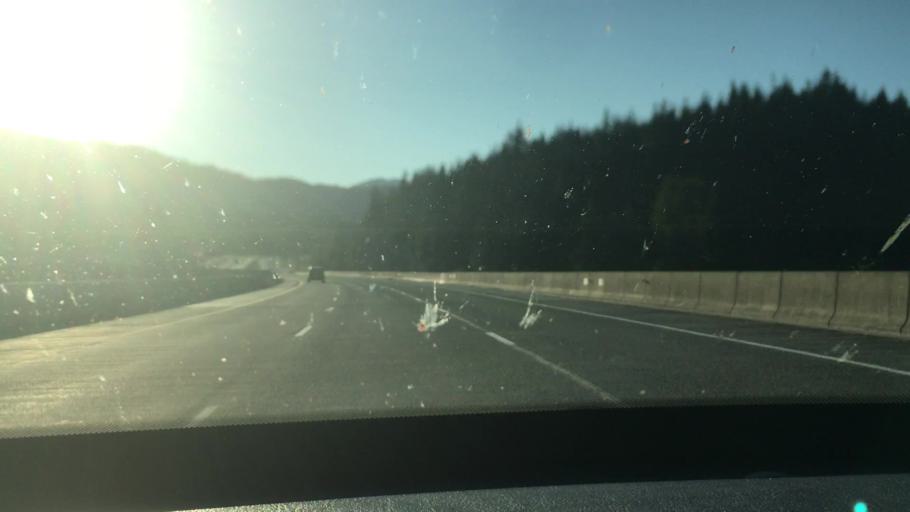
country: US
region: Washington
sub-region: King County
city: Tanner
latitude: 47.3913
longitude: -121.3845
